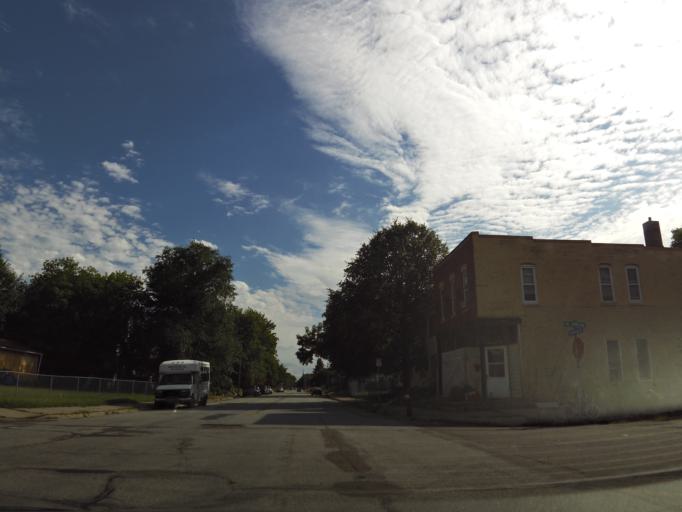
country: US
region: Minnesota
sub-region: Anoka County
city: Columbia Heights
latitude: 45.0124
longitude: -93.2526
